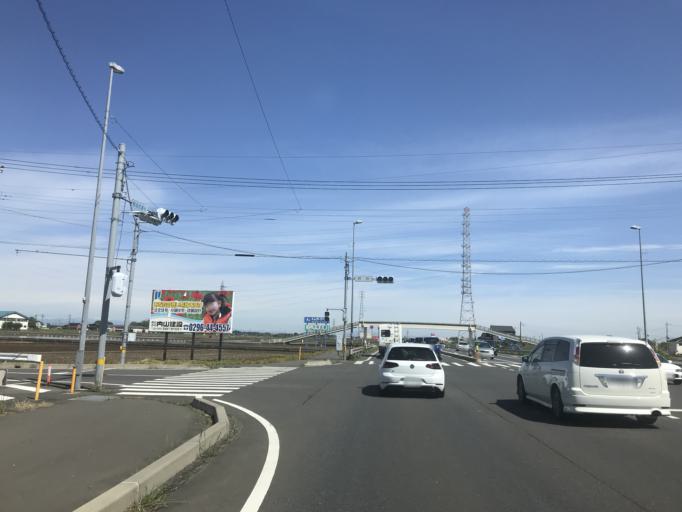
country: JP
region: Ibaraki
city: Ishige
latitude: 36.1715
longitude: 139.9921
